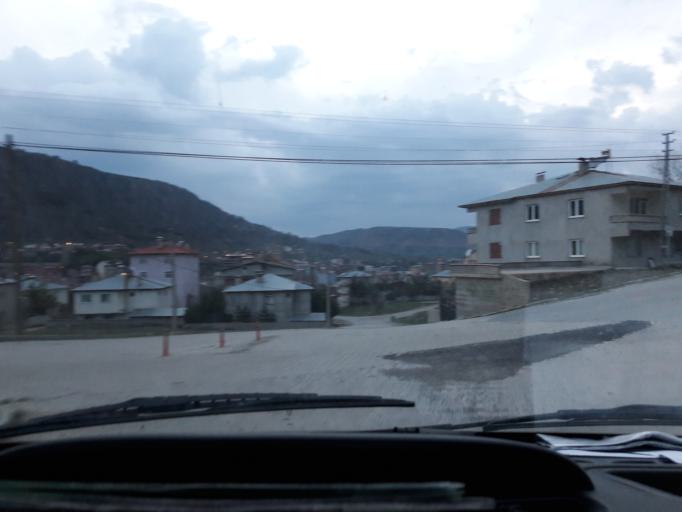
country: TR
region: Giresun
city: Alucra
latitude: 40.3230
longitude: 38.7692
